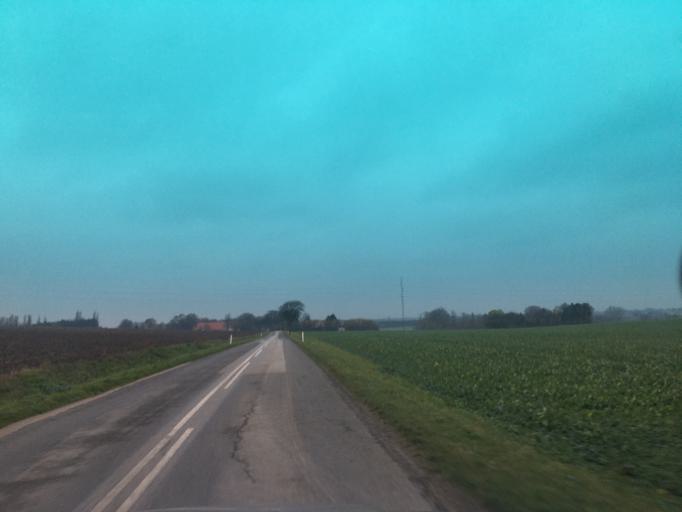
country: DK
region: Zealand
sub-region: Slagelse Kommune
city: Skaelskor
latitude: 55.2603
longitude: 11.4179
